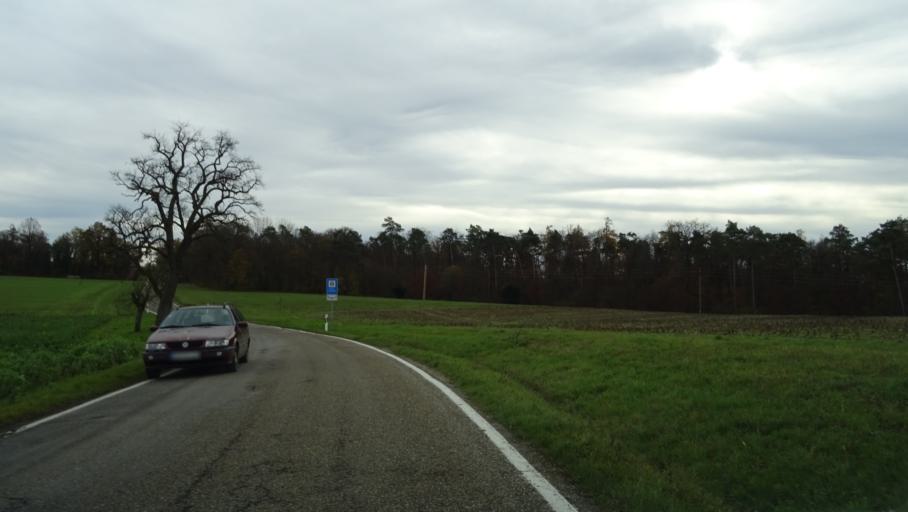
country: DE
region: Baden-Wuerttemberg
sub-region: Karlsruhe Region
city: Obrigheim
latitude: 49.3868
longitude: 9.1010
